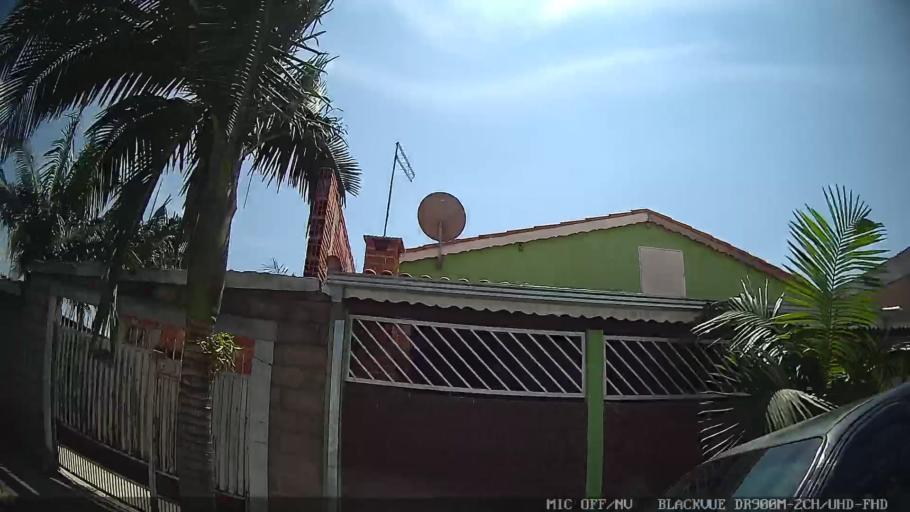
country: BR
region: Sao Paulo
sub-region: Cabreuva
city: Cabreuva
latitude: -23.2539
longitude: -47.0588
